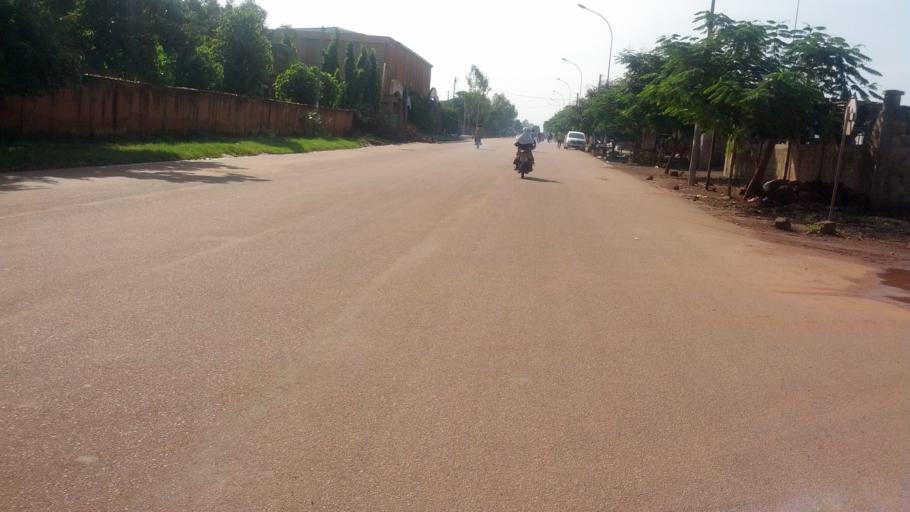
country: BF
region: Centre
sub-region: Kadiogo Province
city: Ouagadougou
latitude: 12.3528
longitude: -1.4910
